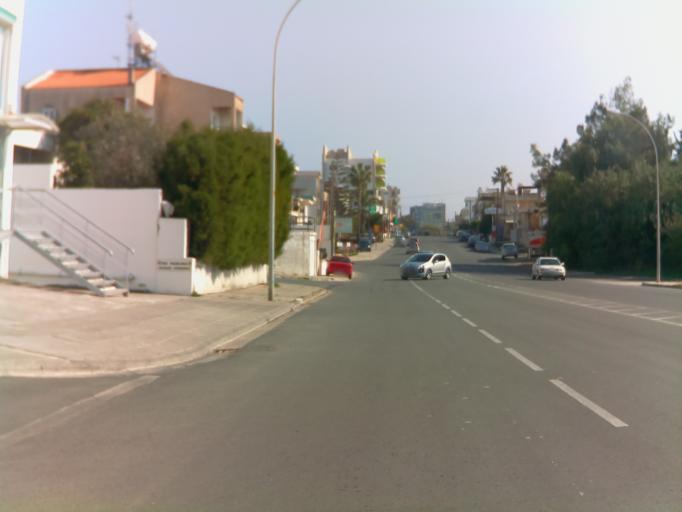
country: CY
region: Larnaka
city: Larnaca
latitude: 34.9112
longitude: 33.6174
